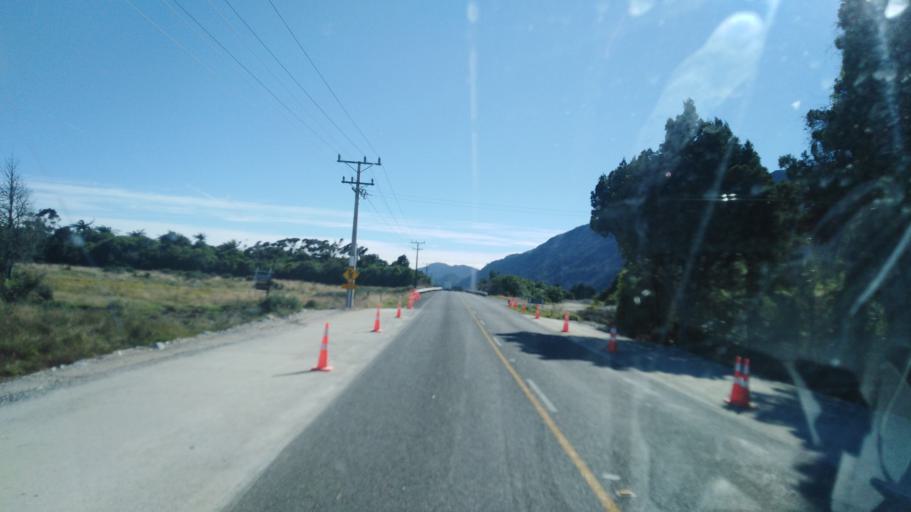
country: NZ
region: West Coast
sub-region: Buller District
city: Westport
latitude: -41.6676
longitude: 171.8088
